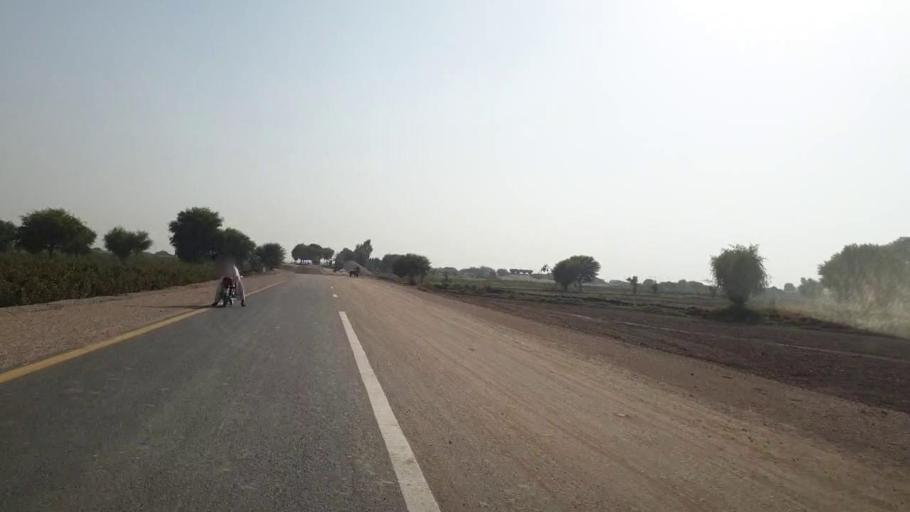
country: PK
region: Sindh
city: Bhan
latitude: 26.5043
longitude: 67.7829
